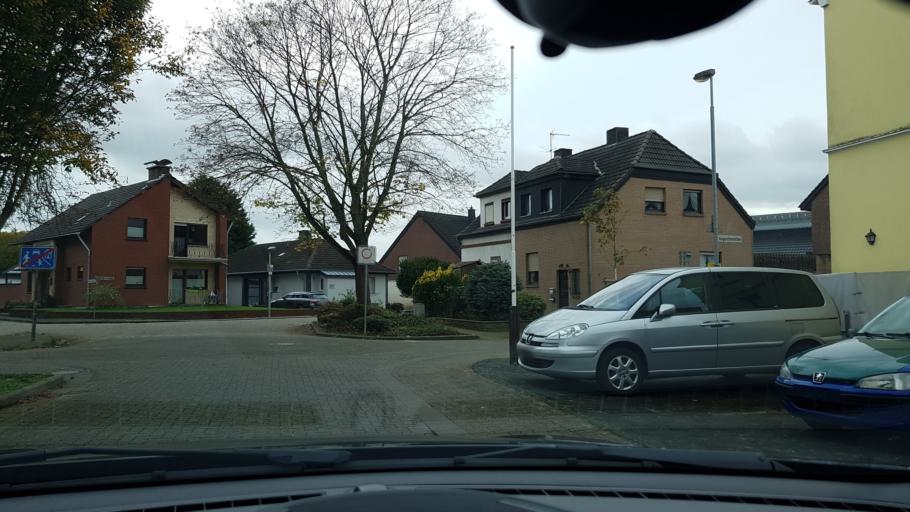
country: DE
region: North Rhine-Westphalia
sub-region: Regierungsbezirk Koln
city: Bedburg
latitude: 51.0010
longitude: 6.5788
